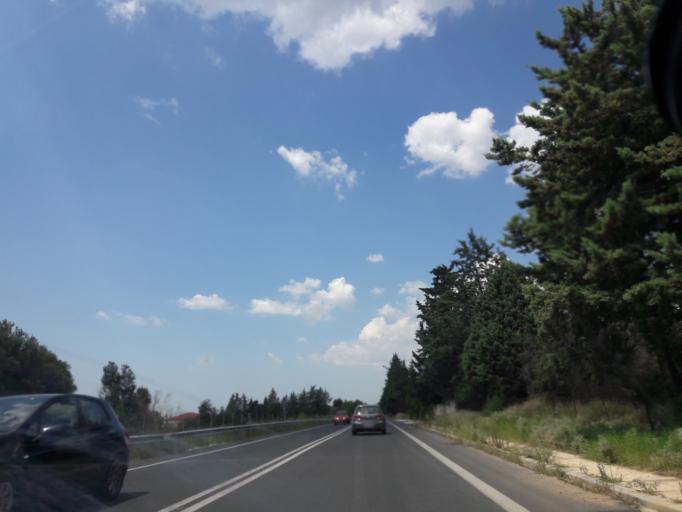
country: GR
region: Central Macedonia
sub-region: Nomos Thessalonikis
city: Souroti
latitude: 40.5096
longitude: 23.0835
